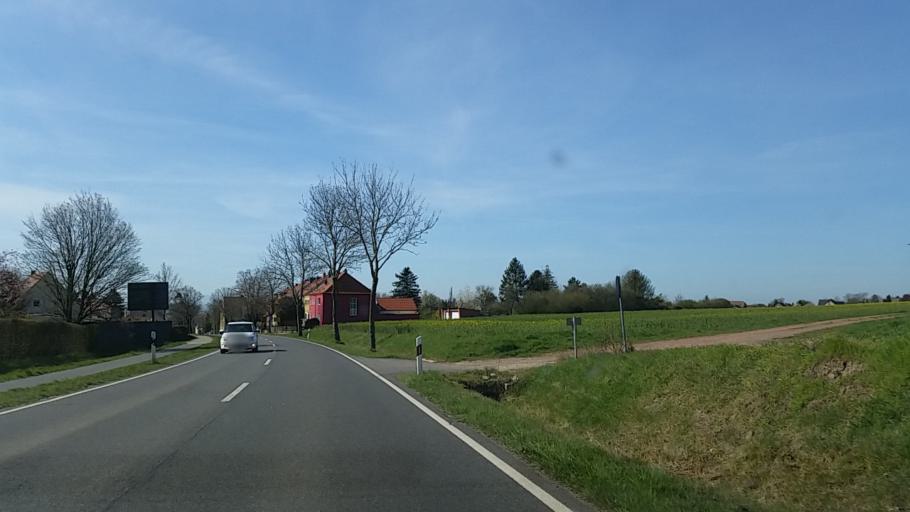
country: DE
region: Lower Saxony
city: Schoningen
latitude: 52.1304
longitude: 10.9451
